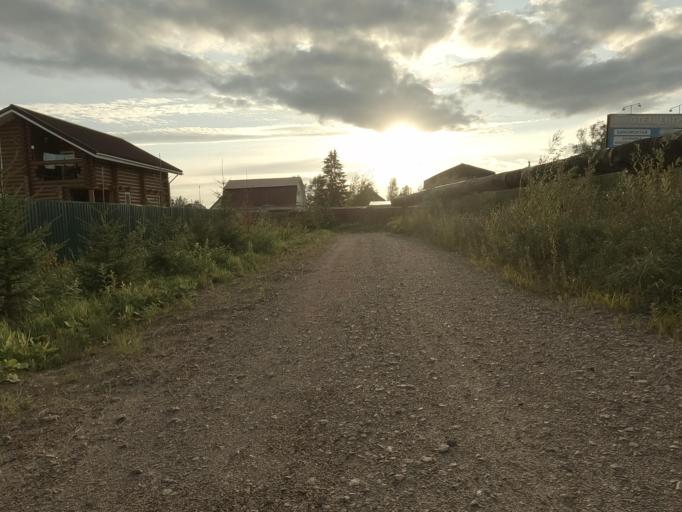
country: RU
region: Leningrad
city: Mga
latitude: 59.7569
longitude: 31.0812
